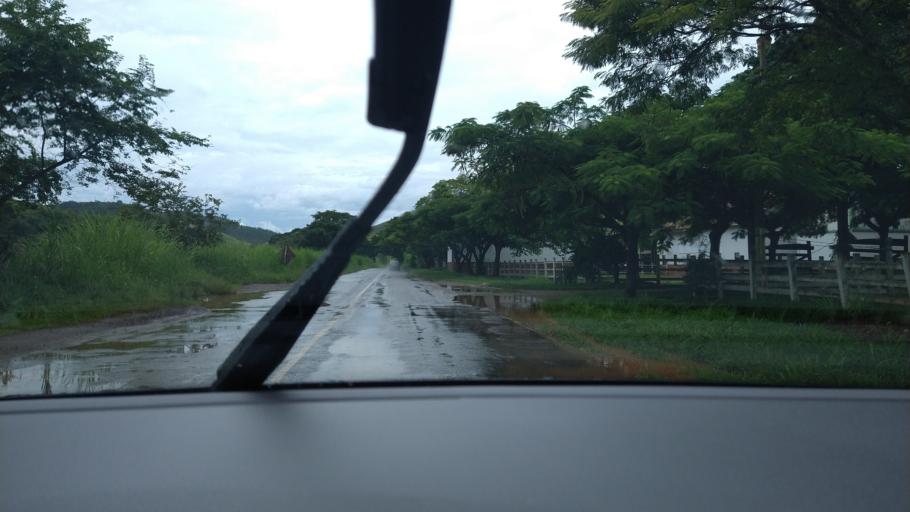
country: BR
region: Minas Gerais
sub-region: Ponte Nova
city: Ponte Nova
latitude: -20.3716
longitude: -42.8948
